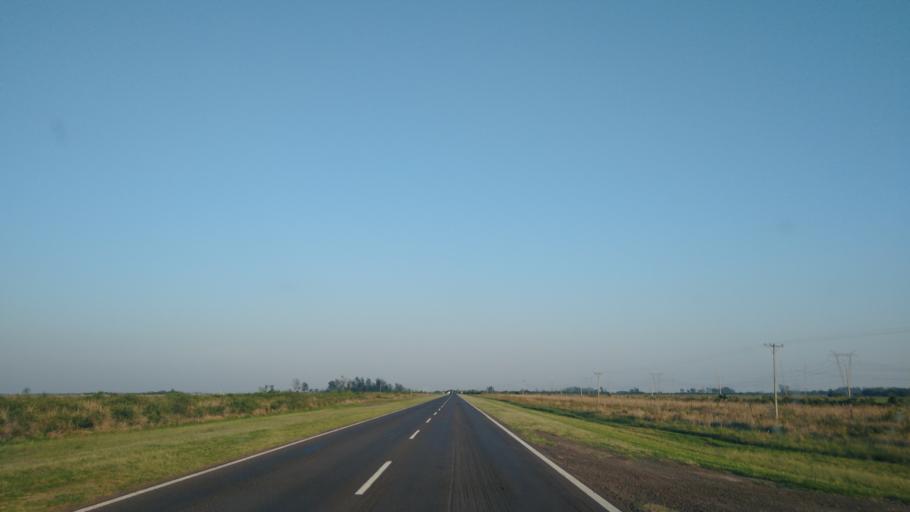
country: PY
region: Neembucu
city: Cerrito
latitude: -27.4194
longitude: -57.6352
